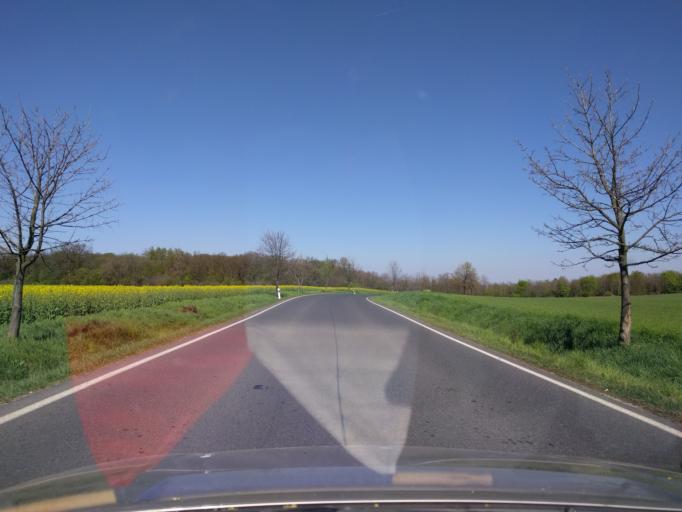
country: CZ
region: Central Bohemia
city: Cesky Brod
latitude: 50.1001
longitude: 14.8610
